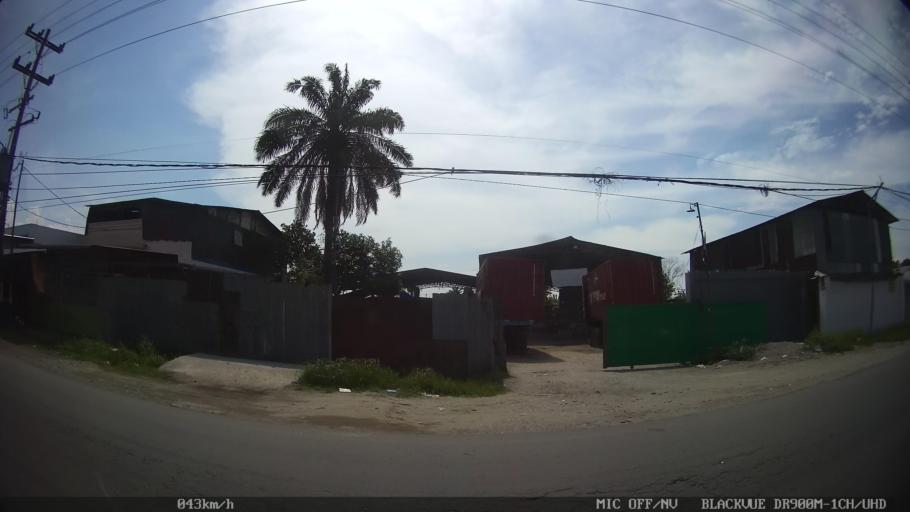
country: ID
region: North Sumatra
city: Labuhan Deli
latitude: 3.6709
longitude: 98.6558
